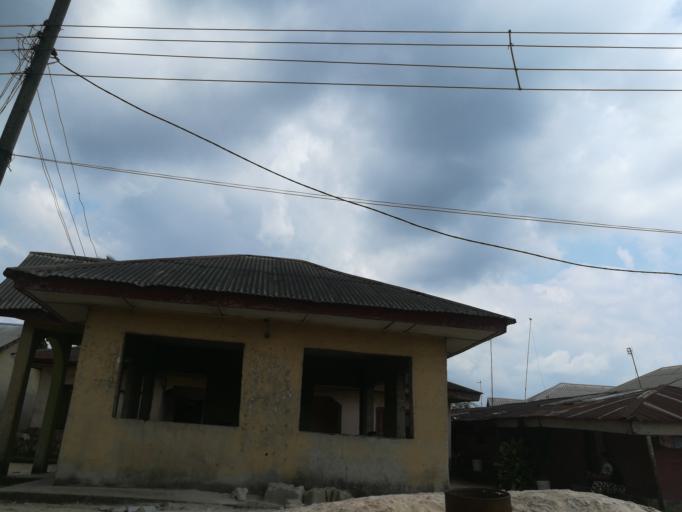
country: NG
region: Rivers
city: Okrika
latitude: 4.7285
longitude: 7.1488
